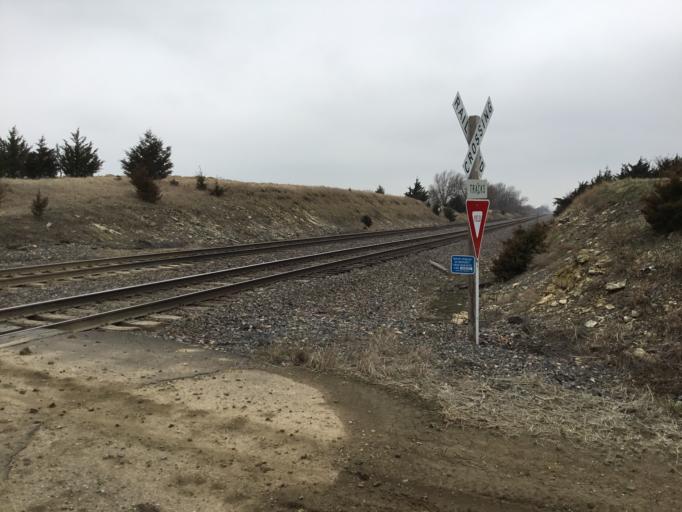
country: US
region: Kansas
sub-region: Dickinson County
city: Herington
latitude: 38.7111
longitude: -96.9089
